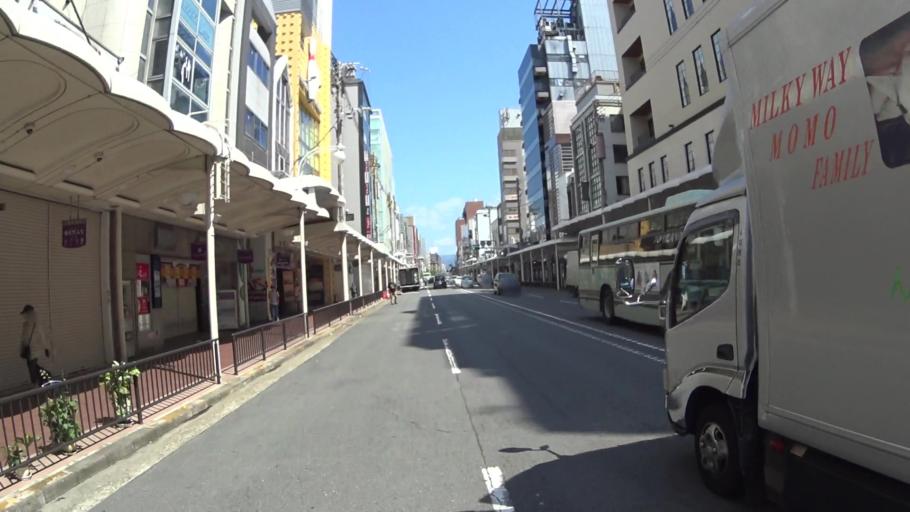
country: JP
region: Kyoto
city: Kyoto
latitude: 35.0058
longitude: 135.7695
